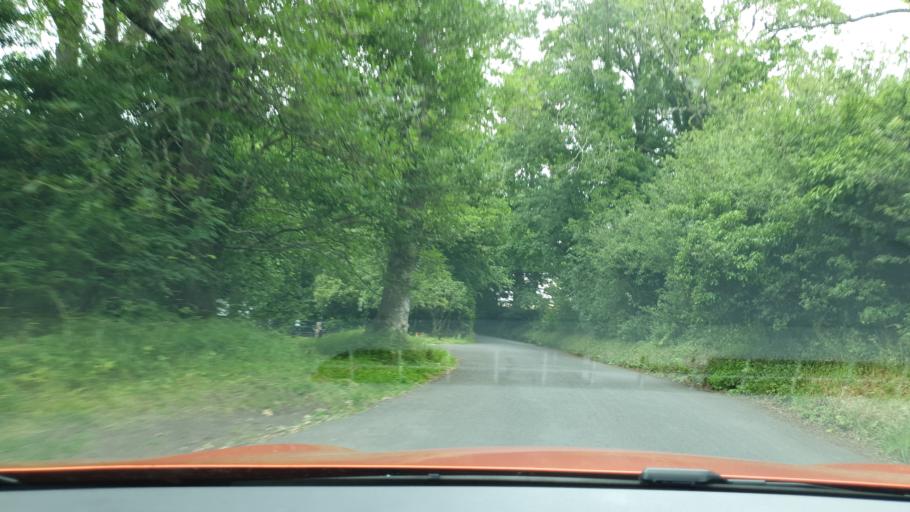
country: GB
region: England
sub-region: Cumbria
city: Penrith
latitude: 54.5881
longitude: -2.8438
